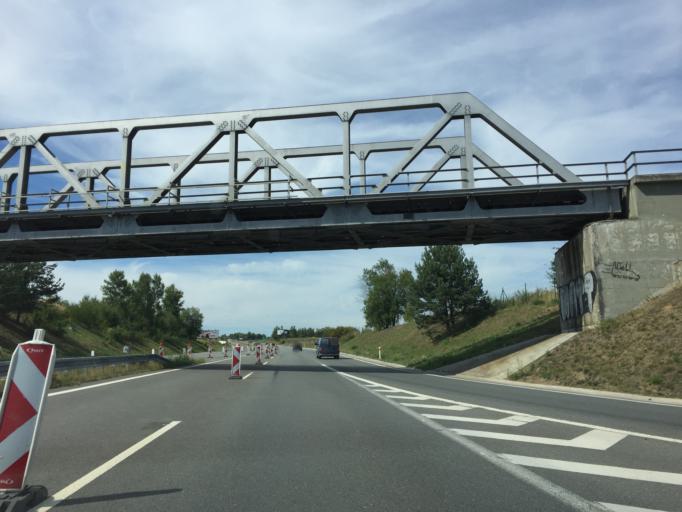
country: CZ
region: Jihocesky
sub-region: Okres Tabor
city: Sezimovo Usti
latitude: 49.4060
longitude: 14.7178
